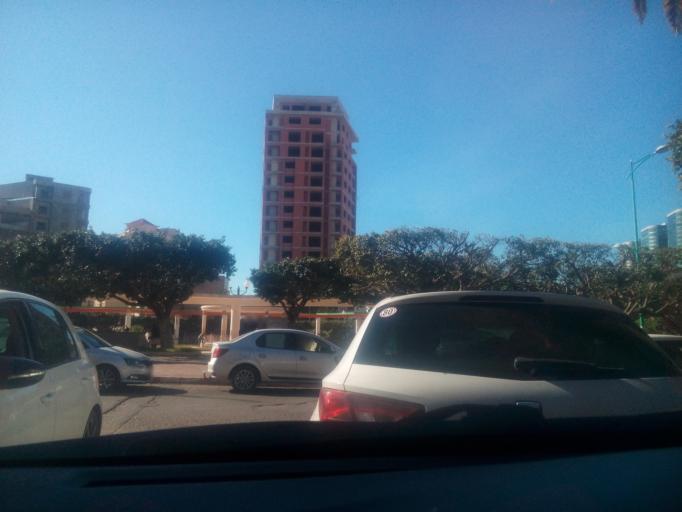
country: DZ
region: Oran
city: Oran
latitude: 35.7119
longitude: -0.6195
